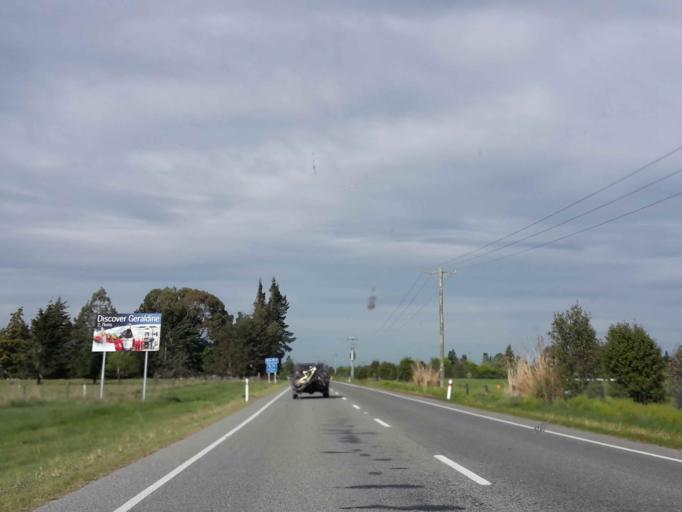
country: NZ
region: Canterbury
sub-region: Timaru District
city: Pleasant Point
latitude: -44.1131
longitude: 171.2186
